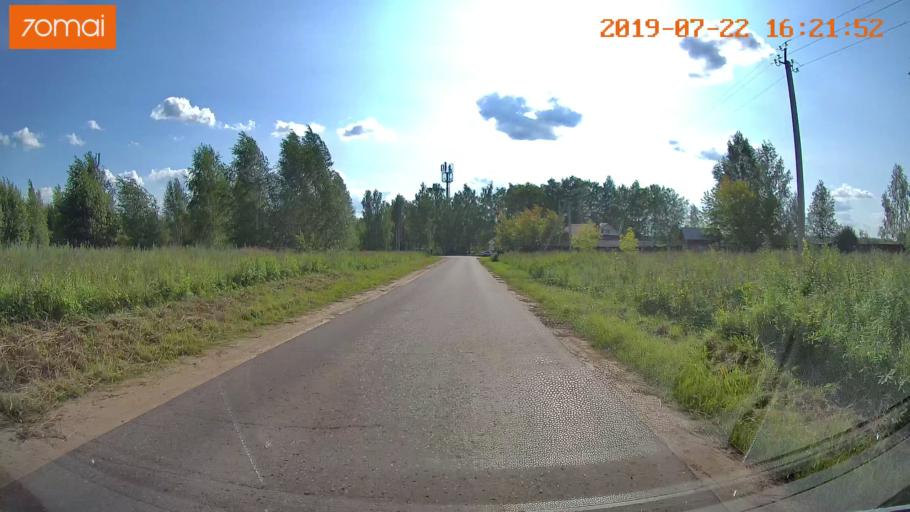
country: RU
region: Ivanovo
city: Novo-Talitsy
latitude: 57.0602
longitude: 40.8796
